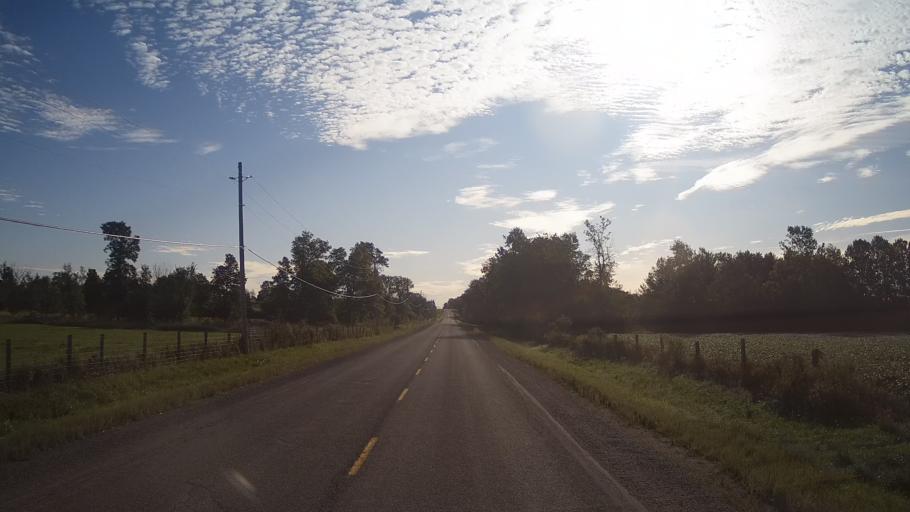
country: US
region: New York
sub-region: Jefferson County
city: Alexandria Bay
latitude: 44.4043
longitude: -76.0369
